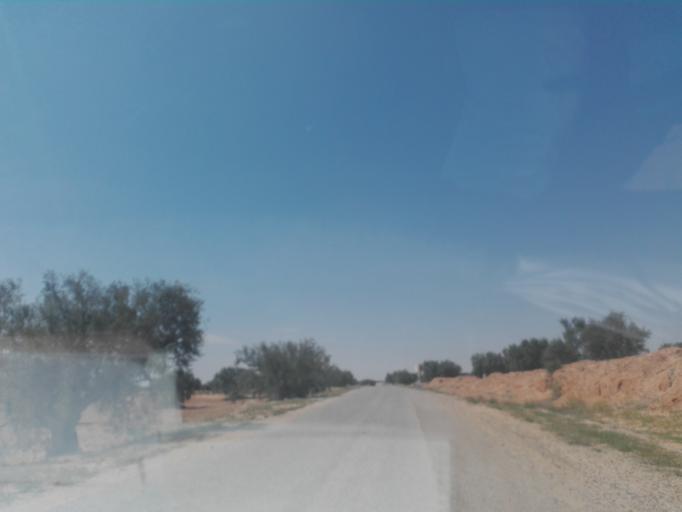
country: TN
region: Safaqis
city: Bi'r `Ali Bin Khalifah
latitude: 34.6269
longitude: 10.3724
